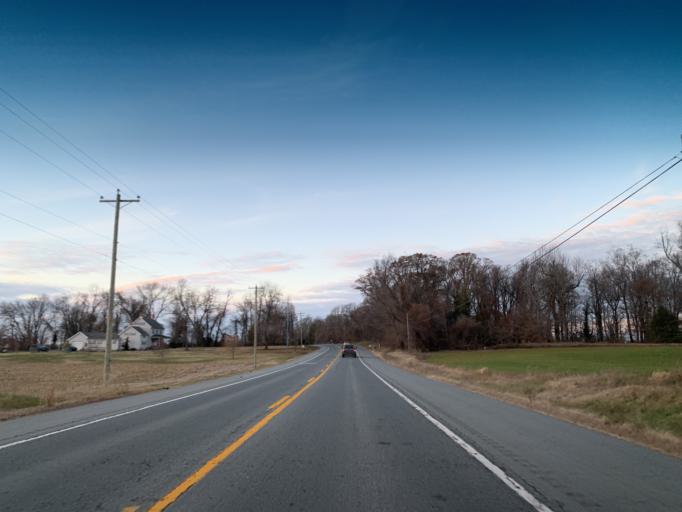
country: US
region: Delaware
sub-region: New Castle County
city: Middletown
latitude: 39.4527
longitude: -75.8700
